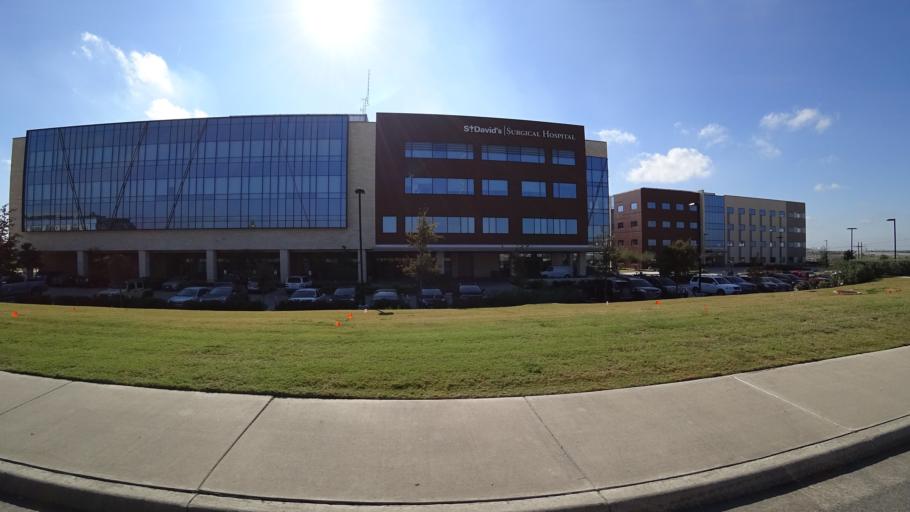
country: US
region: Texas
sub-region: Williamson County
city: Round Rock
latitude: 30.4778
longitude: -97.6909
